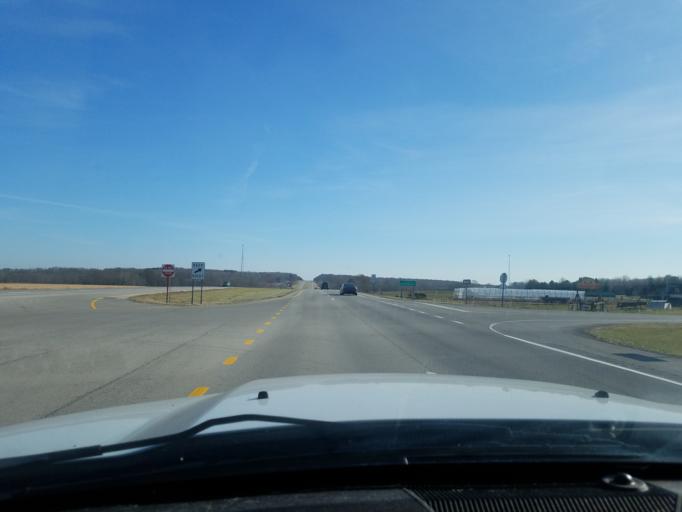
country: US
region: Ohio
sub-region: Adams County
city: Winchester
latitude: 38.9343
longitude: -83.6332
